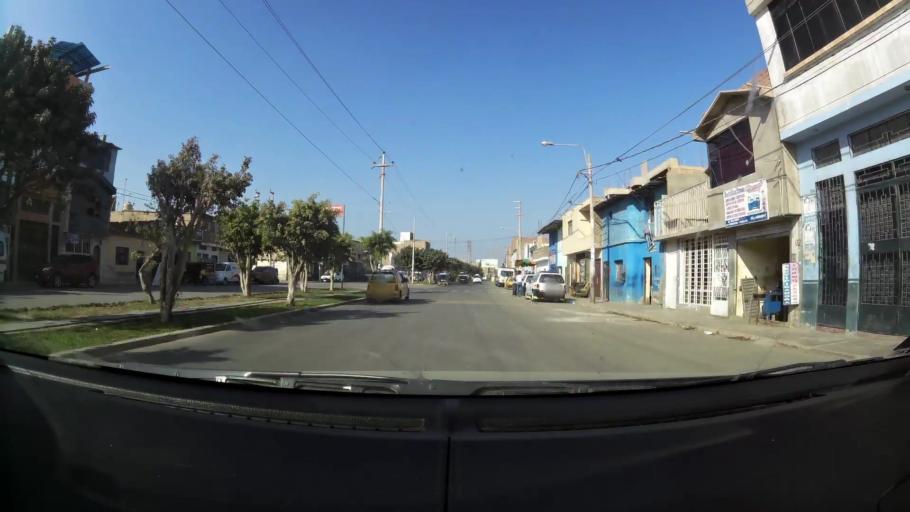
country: PE
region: Lambayeque
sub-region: Provincia de Chiclayo
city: Chiclayo
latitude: -6.7629
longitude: -79.8476
